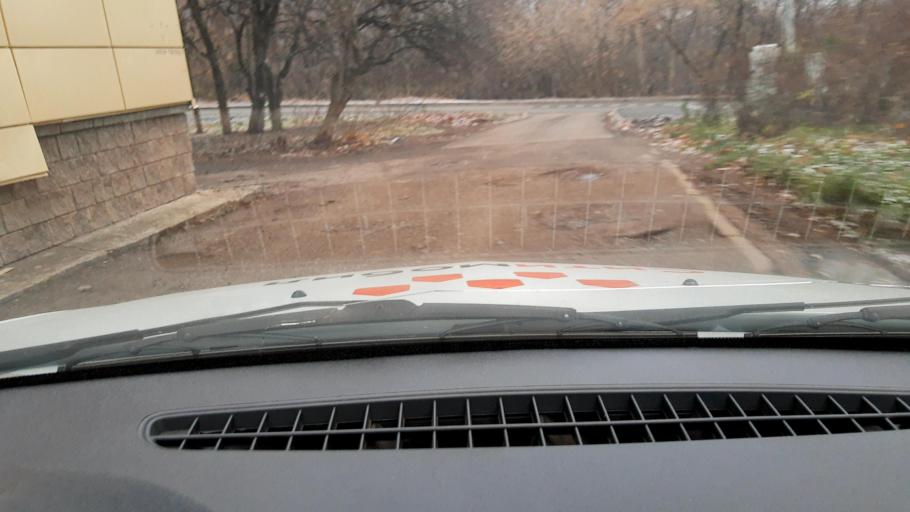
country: RU
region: Bashkortostan
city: Ufa
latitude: 54.7932
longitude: 56.0294
